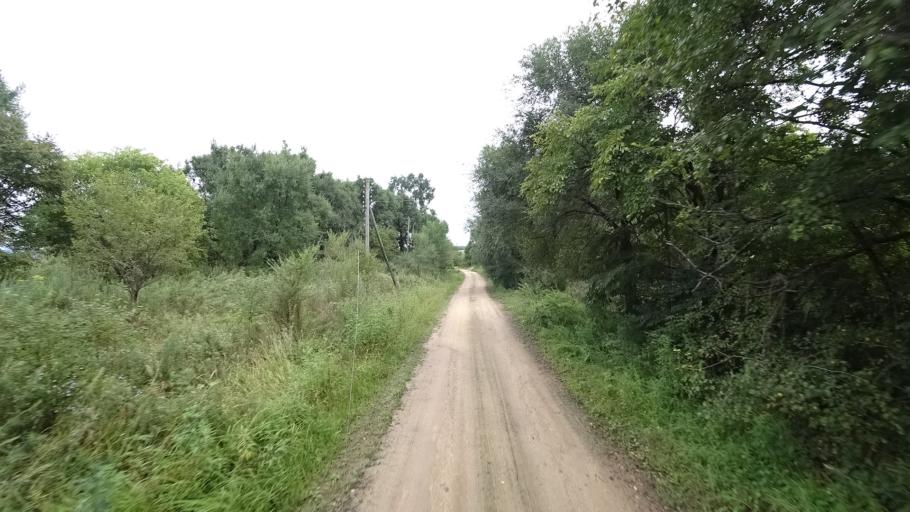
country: RU
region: Primorskiy
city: Rettikhovka
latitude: 44.1316
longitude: 132.6345
